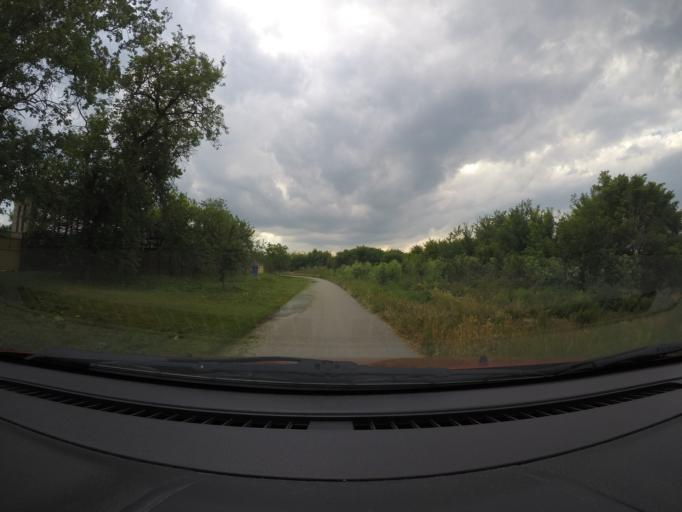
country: RS
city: Uzdin
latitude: 45.2055
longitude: 20.6139
